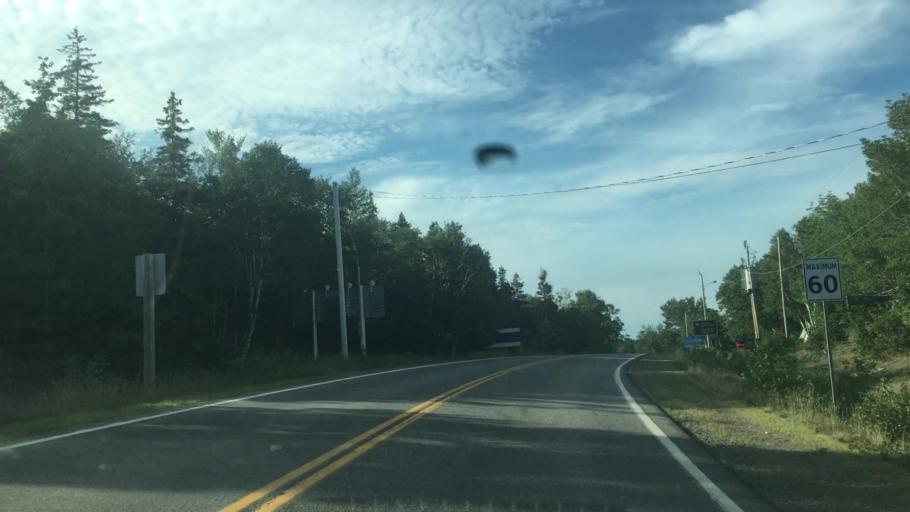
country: CA
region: Nova Scotia
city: Sydney Mines
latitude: 46.8187
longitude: -60.7955
